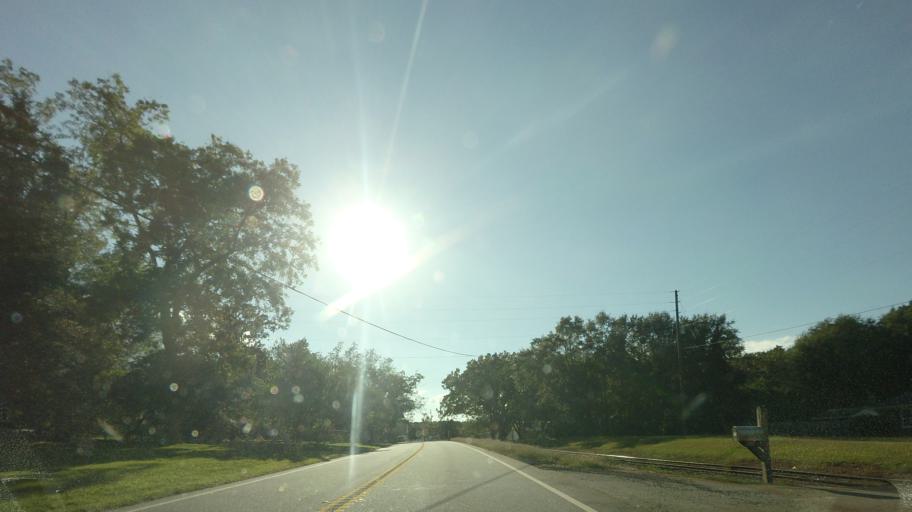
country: US
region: Georgia
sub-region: Upson County
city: Hannahs Mill
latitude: 32.9646
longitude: -84.2380
